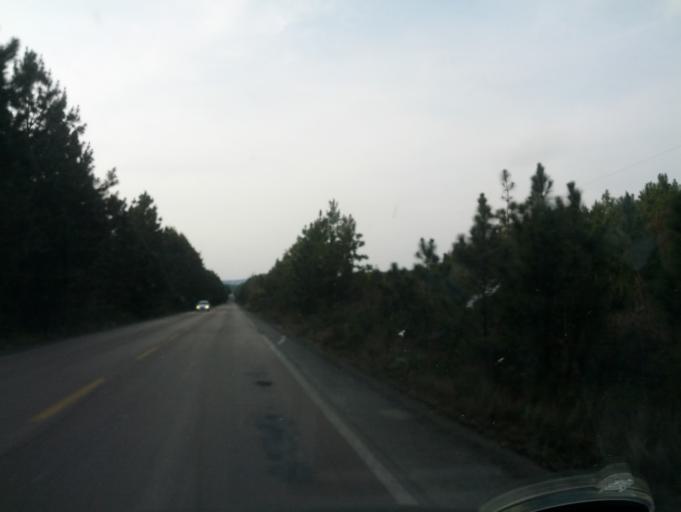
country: BR
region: Santa Catarina
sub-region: Otacilio Costa
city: Otacilio Costa
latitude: -27.3833
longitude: -50.1343
